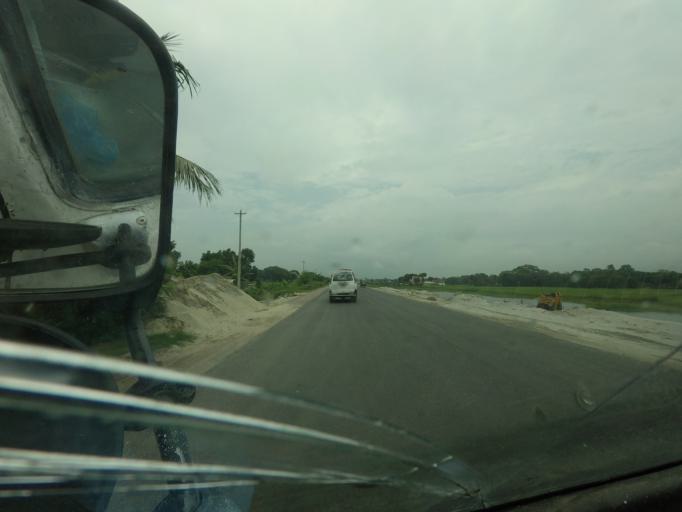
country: BD
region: Dhaka
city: Char Bhadrasan
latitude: 23.3855
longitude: 89.9949
